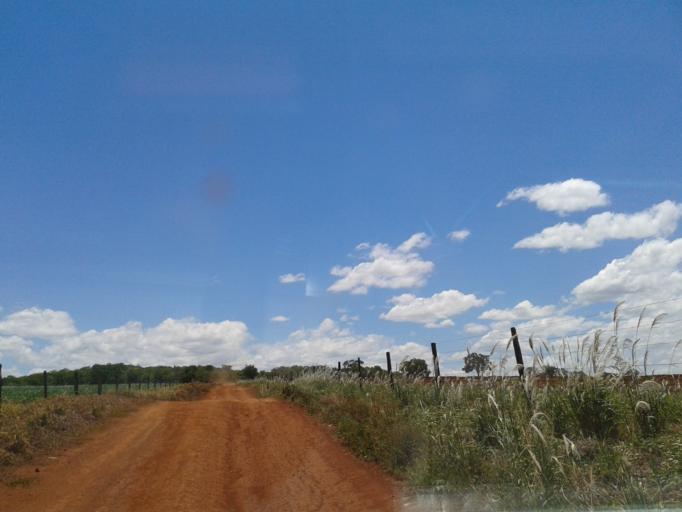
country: BR
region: Minas Gerais
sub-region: Centralina
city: Centralina
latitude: -18.6799
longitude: -49.2269
